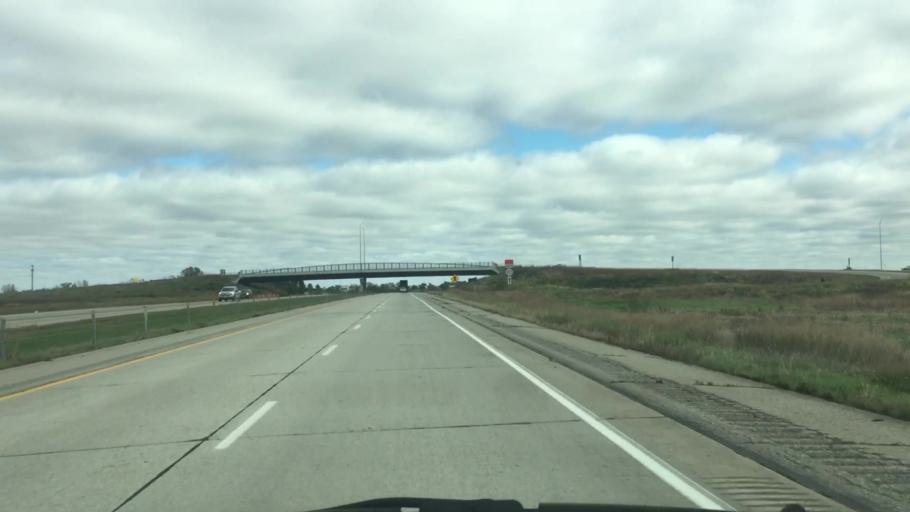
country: US
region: Iowa
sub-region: Polk County
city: Altoona
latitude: 41.6662
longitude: -93.4678
